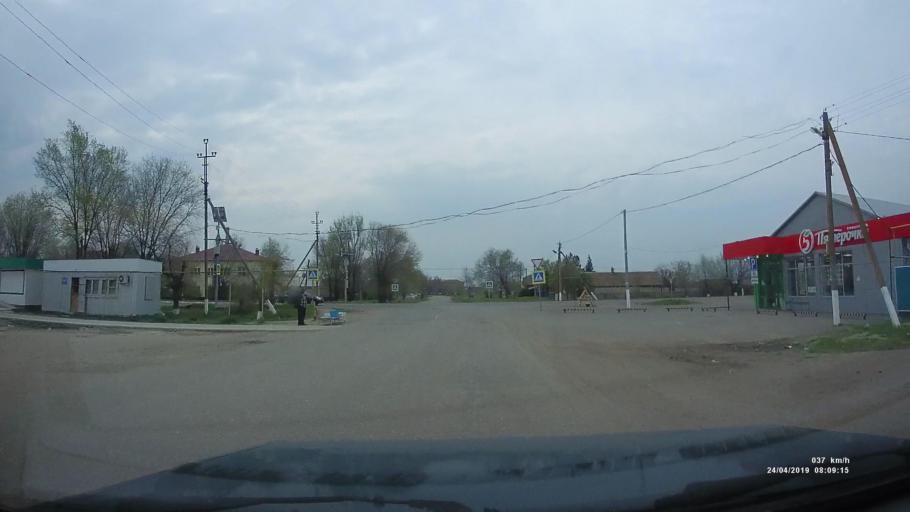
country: RU
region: Kalmykiya
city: Priyutnoye
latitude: 46.0961
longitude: 43.5050
